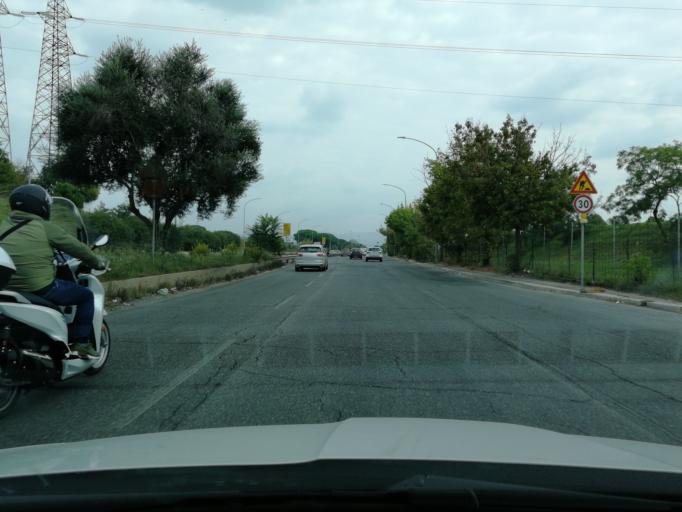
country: IT
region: Latium
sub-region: Citta metropolitana di Roma Capitale
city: Ciampino
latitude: 41.8480
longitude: 12.5762
